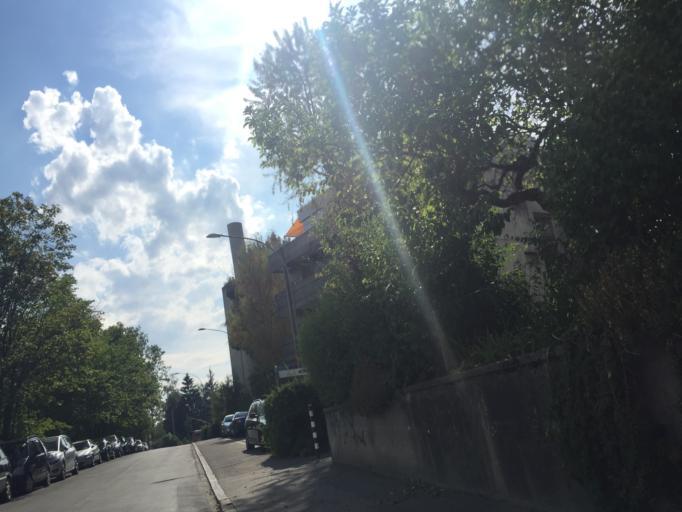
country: CH
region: Bern
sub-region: Bern-Mittelland District
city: Bern
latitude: 46.9521
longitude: 7.4246
